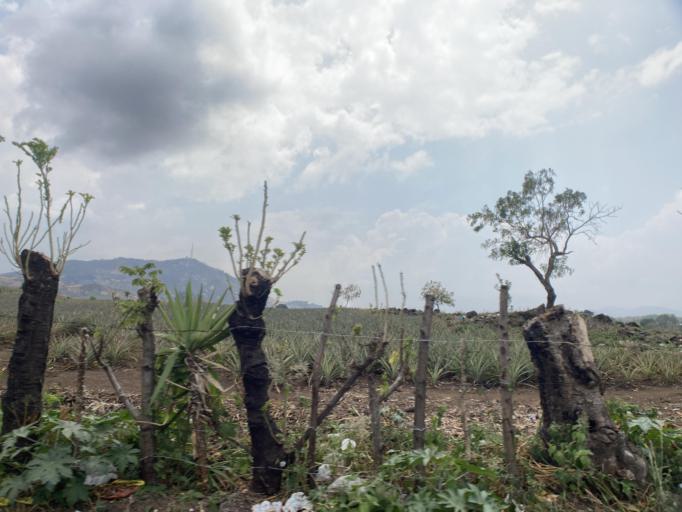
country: GT
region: Guatemala
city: Fraijanes
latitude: 14.3653
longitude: -90.4953
